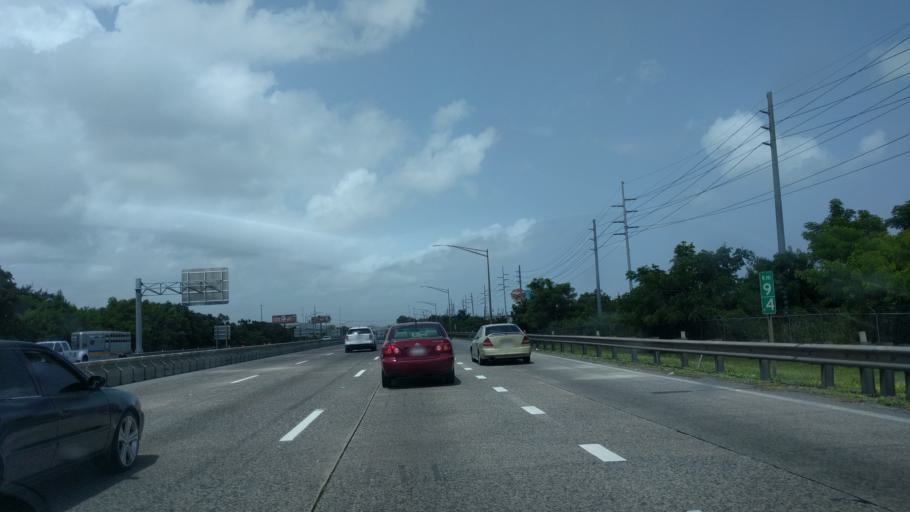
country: PR
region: Catano
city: Catano
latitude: 18.4229
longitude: -66.1326
